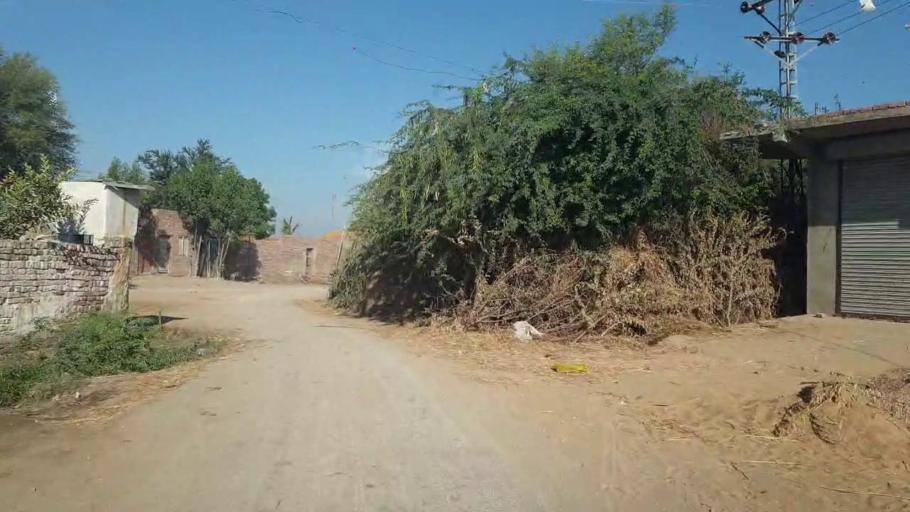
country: PK
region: Sindh
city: Talhar
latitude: 24.8915
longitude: 68.8135
